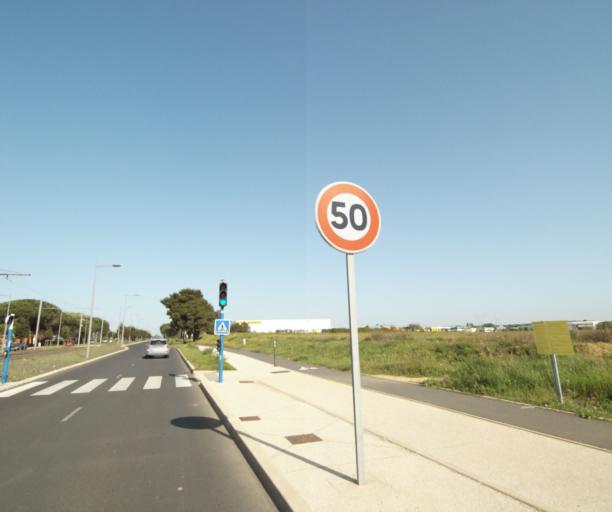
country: FR
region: Languedoc-Roussillon
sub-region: Departement de l'Herault
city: Perols
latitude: 43.5783
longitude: 3.9351
